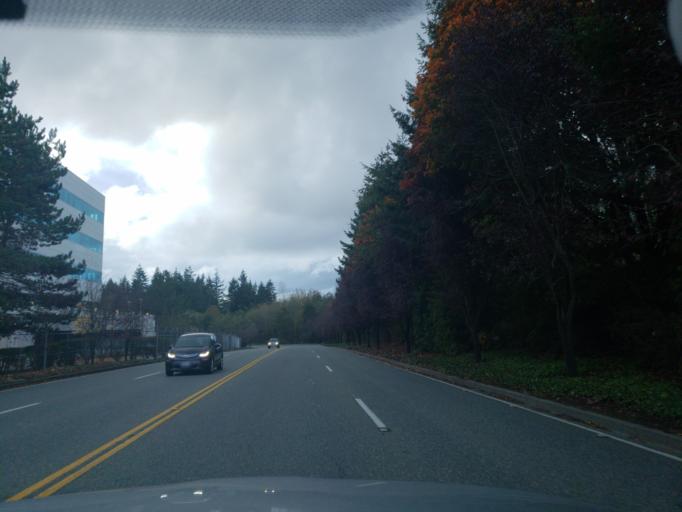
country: US
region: Washington
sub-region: Snohomish County
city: Mukilteo
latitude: 47.9327
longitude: -122.2630
